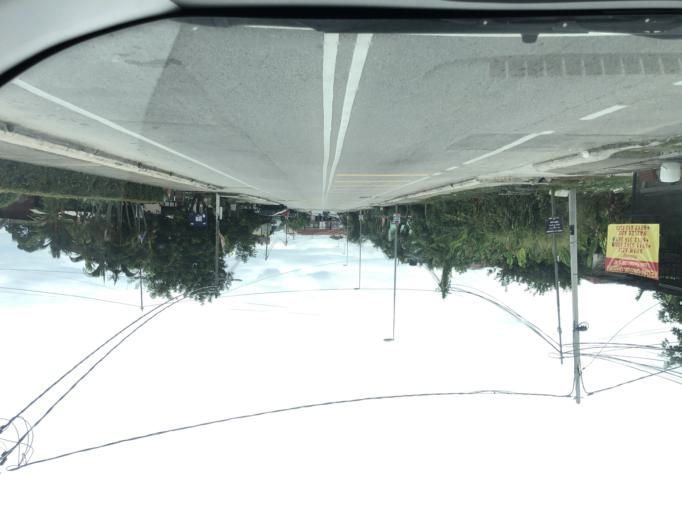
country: MY
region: Putrajaya
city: Putrajaya
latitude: 2.9216
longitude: 101.7583
